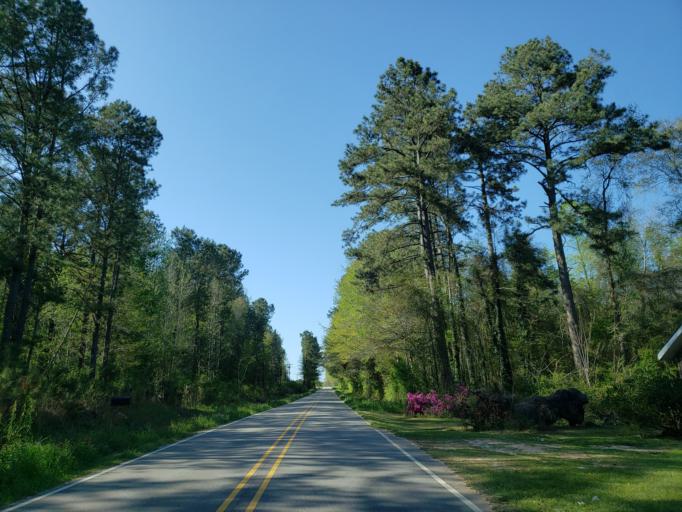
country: US
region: Mississippi
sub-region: Covington County
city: Collins
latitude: 31.6024
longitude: -89.3785
